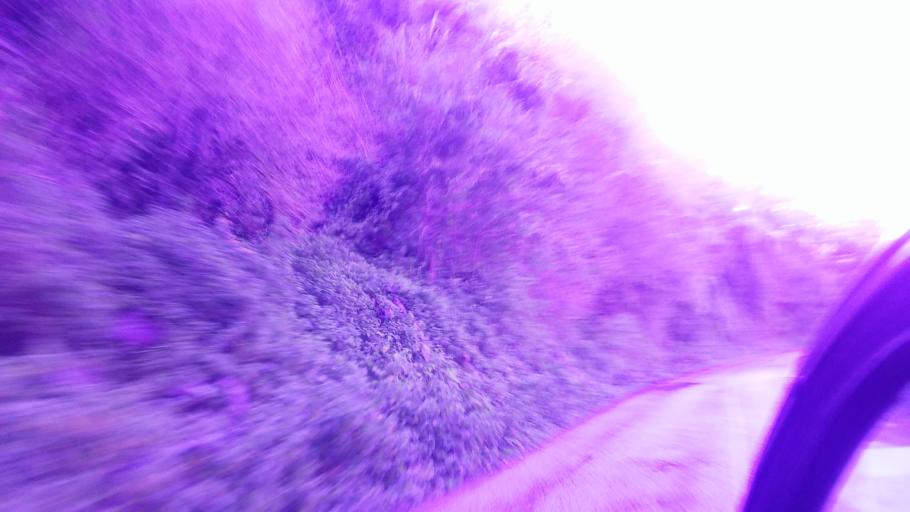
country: IT
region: Latium
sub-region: Provincia di Rieti
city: Amatrice
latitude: 42.6306
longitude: 13.2895
